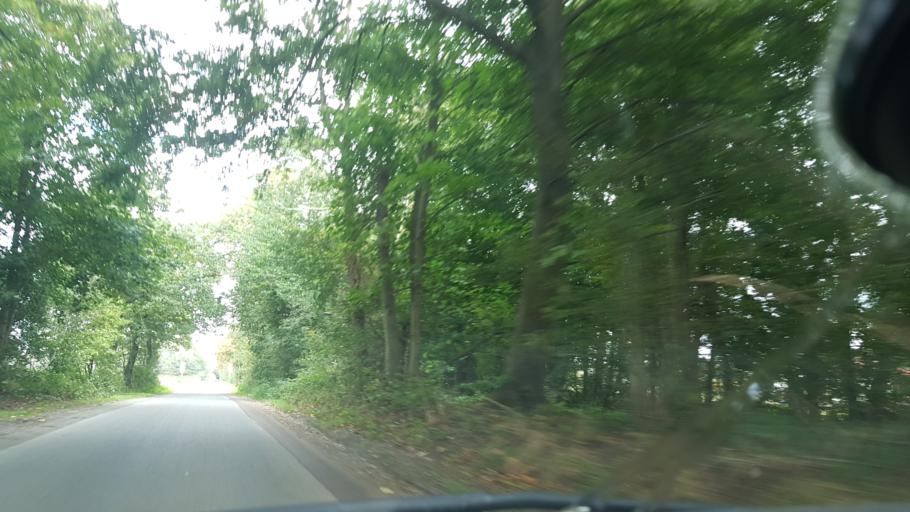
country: DK
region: South Denmark
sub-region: Vejen Kommune
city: Brorup
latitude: 55.4803
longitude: 8.9793
